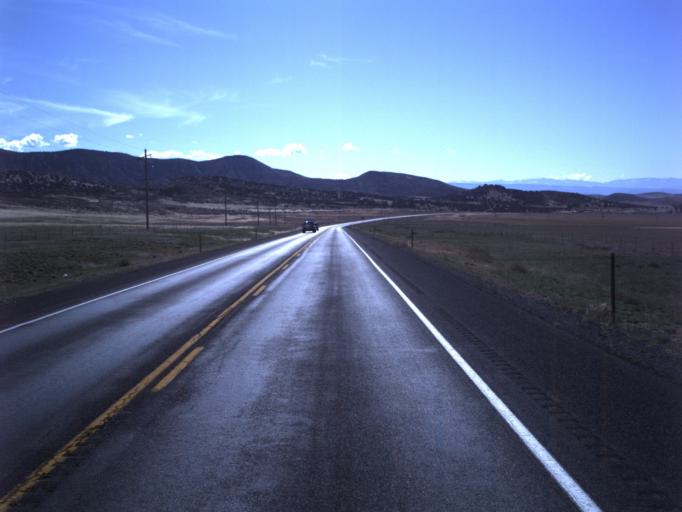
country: US
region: Utah
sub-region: Sanpete County
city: Gunnison
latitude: 39.2429
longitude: -111.8523
